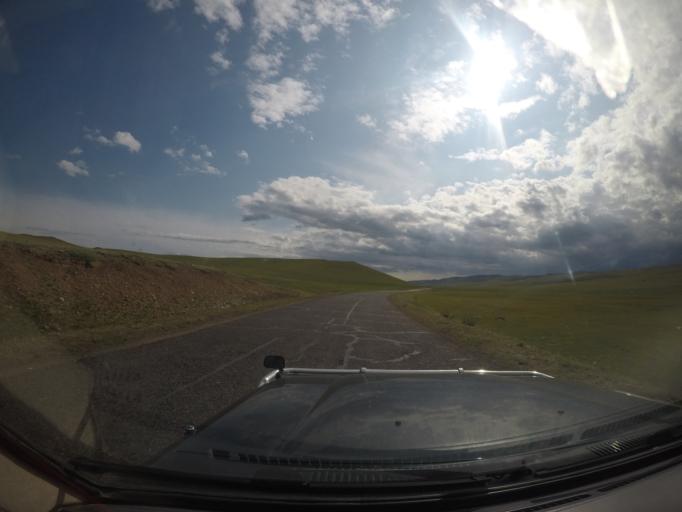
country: MN
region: Hentiy
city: Modot
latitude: 47.7679
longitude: 108.6484
